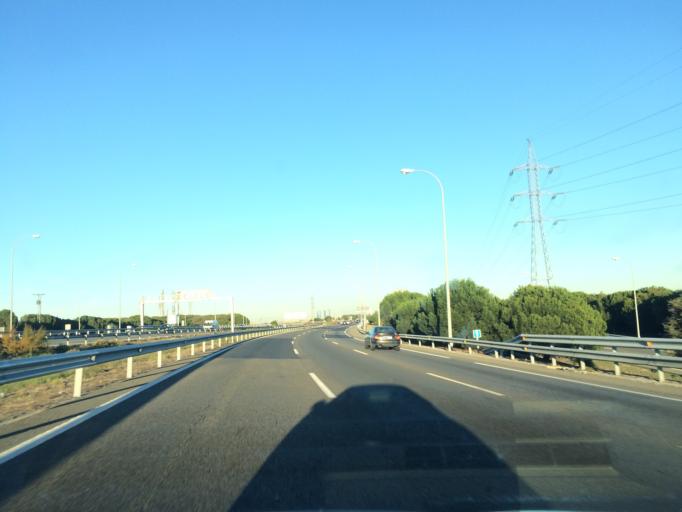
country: ES
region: Madrid
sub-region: Provincia de Madrid
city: Pozuelo de Alarcon
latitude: 40.4070
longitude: -3.8274
